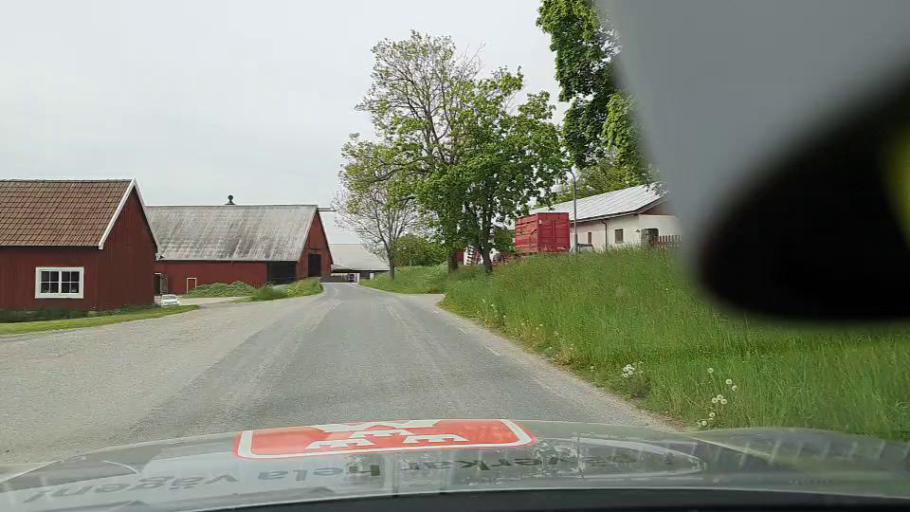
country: SE
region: Soedermanland
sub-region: Flens Kommun
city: Halleforsnas
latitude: 59.0984
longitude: 16.4959
